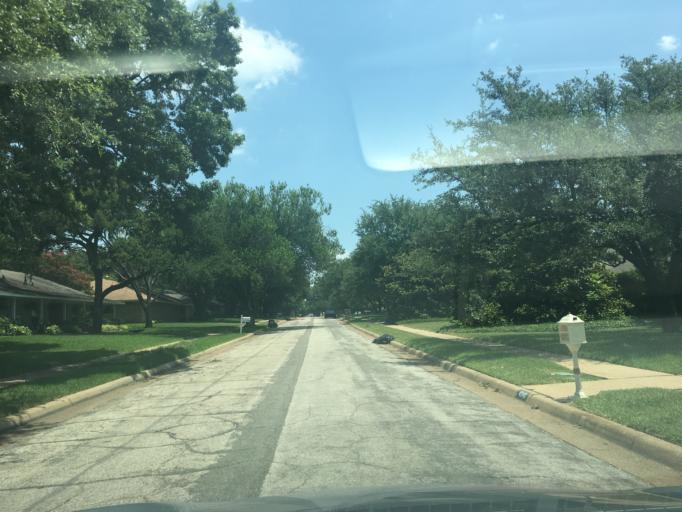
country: US
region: Texas
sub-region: Dallas County
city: Addison
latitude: 32.9147
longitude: -96.8419
